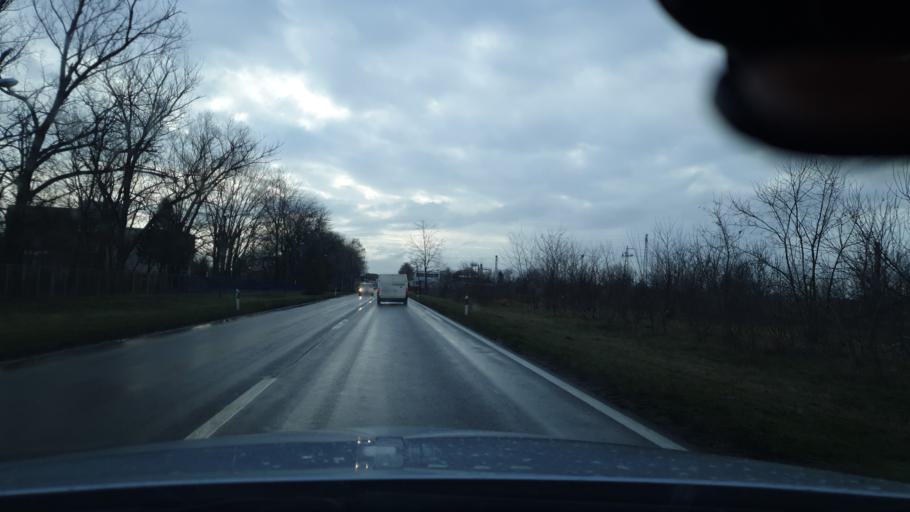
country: RS
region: Autonomna Pokrajina Vojvodina
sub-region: Juznobanatski Okrug
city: Kovin
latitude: 44.7566
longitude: 20.9640
